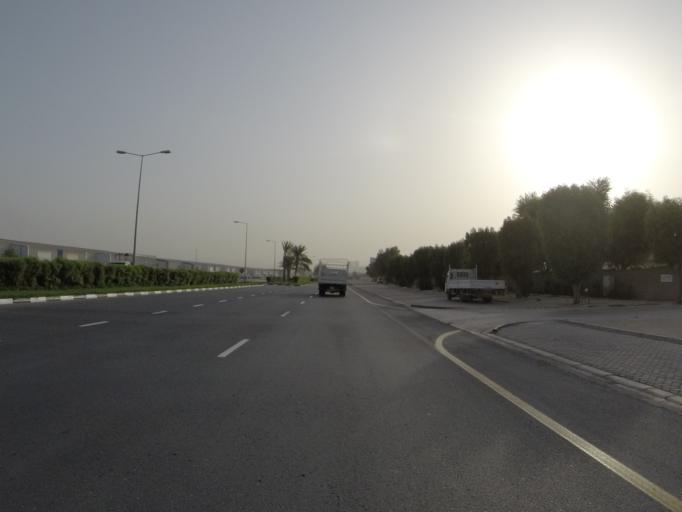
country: AE
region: Dubai
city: Dubai
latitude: 24.9623
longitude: 55.0674
